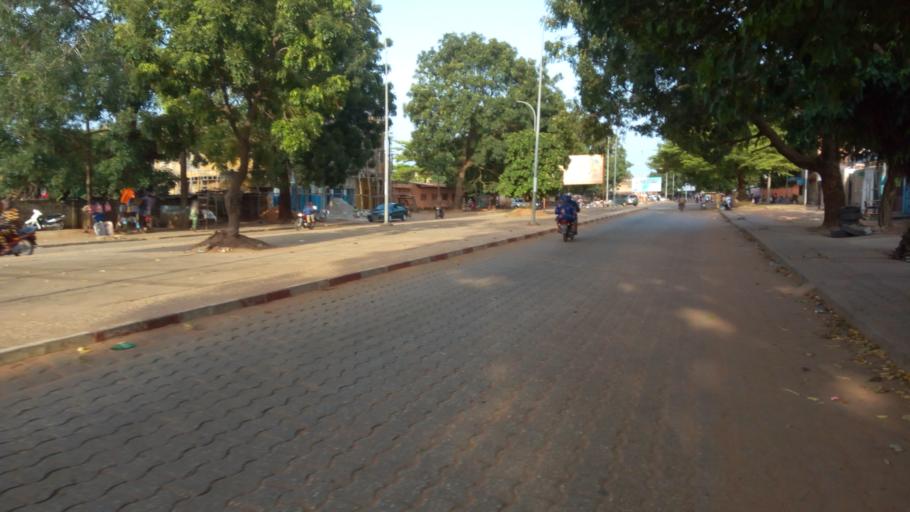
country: BJ
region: Queme
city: Porto-Novo
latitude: 6.4849
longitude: 2.6245
